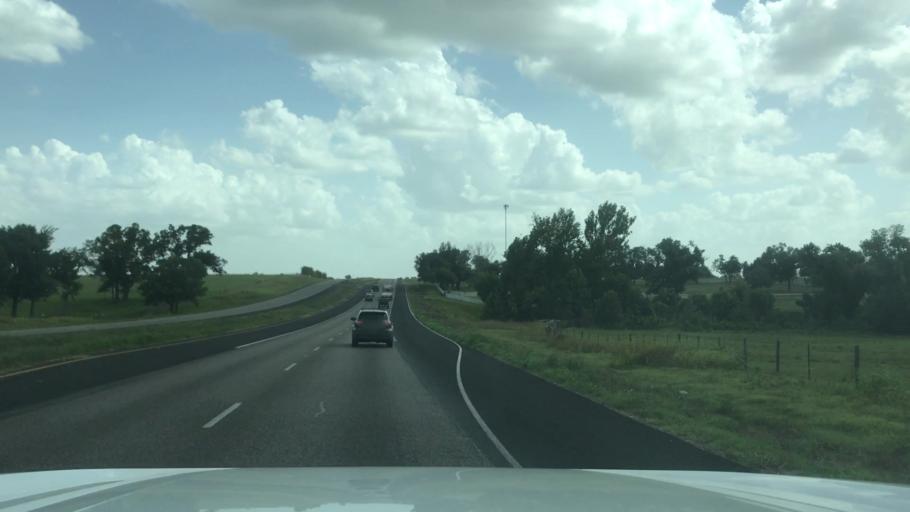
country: US
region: Texas
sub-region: Grimes County
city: Navasota
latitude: 30.3209
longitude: -96.0474
